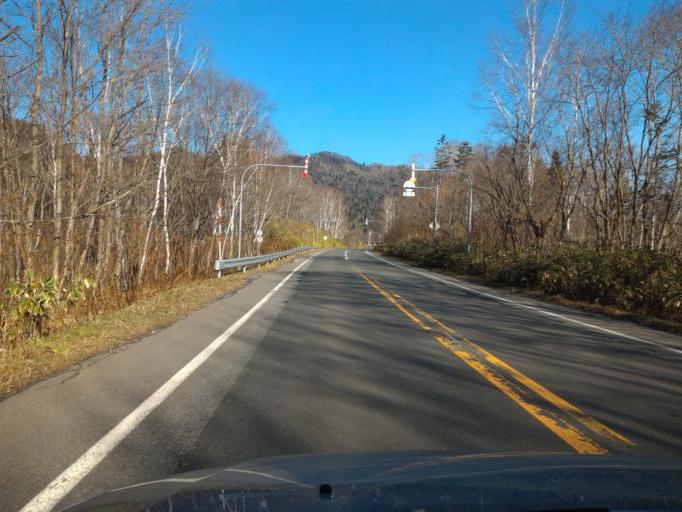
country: JP
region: Hokkaido
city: Ashibetsu
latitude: 43.2992
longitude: 142.1127
